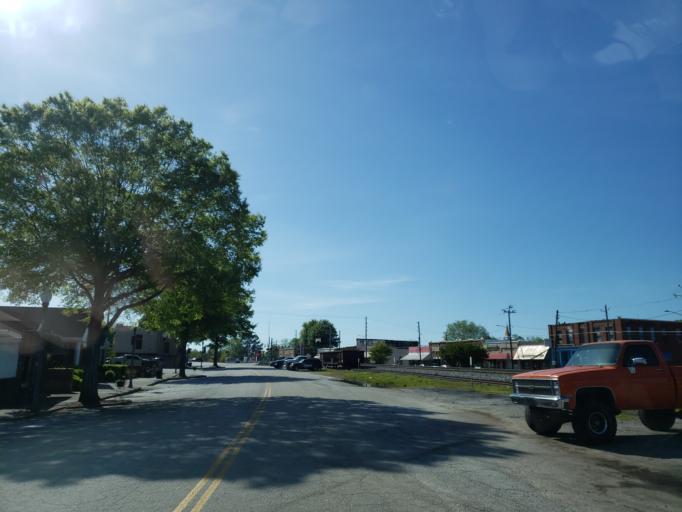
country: US
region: Georgia
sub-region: Haralson County
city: Tallapoosa
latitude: 33.7437
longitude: -85.2860
